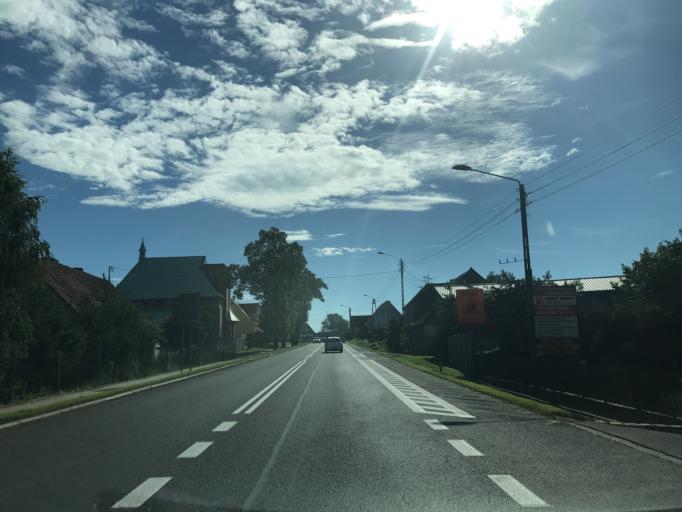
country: PL
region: West Pomeranian Voivodeship
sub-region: Powiat slawienski
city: Slawno
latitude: 54.3651
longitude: 16.7095
